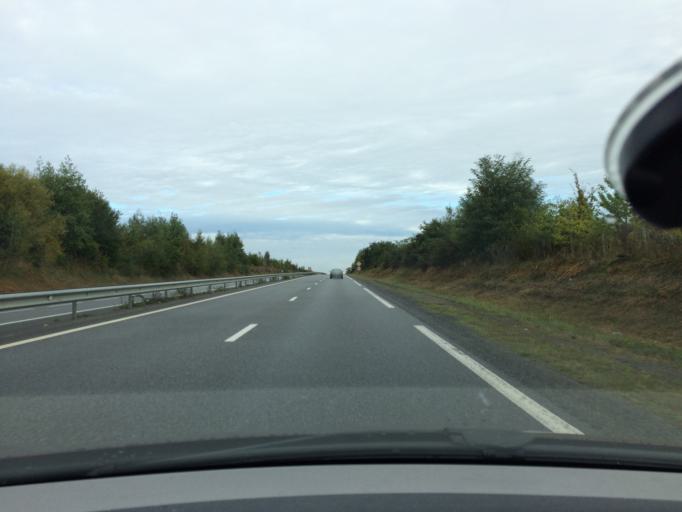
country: FR
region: Brittany
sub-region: Departement d'Ille-et-Vilaine
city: Saint-Armel
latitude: 48.0037
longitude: -1.5940
